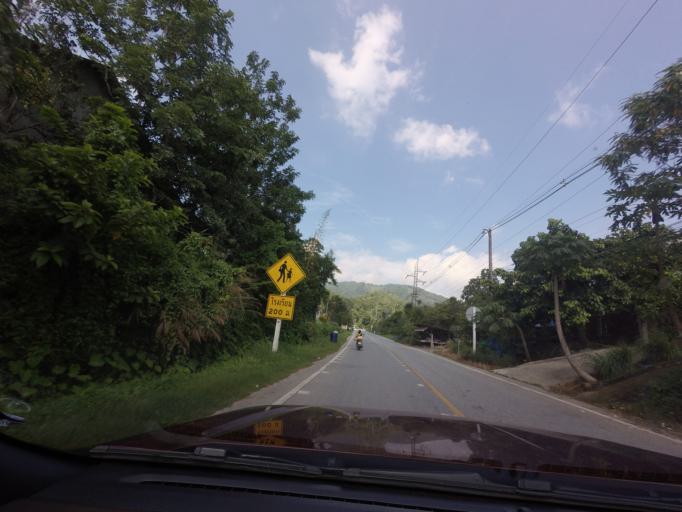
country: TH
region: Yala
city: Betong
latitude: 5.9191
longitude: 101.1783
